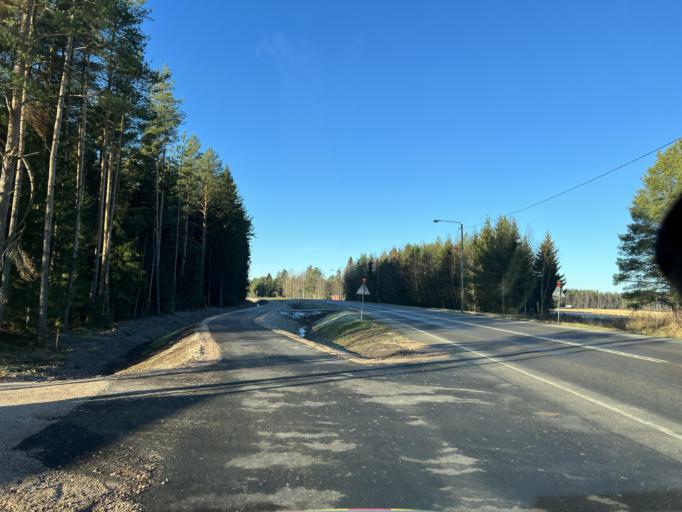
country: FI
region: Northern Ostrobothnia
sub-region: Nivala-Haapajaervi
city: Nivala
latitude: 63.9498
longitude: 24.9196
